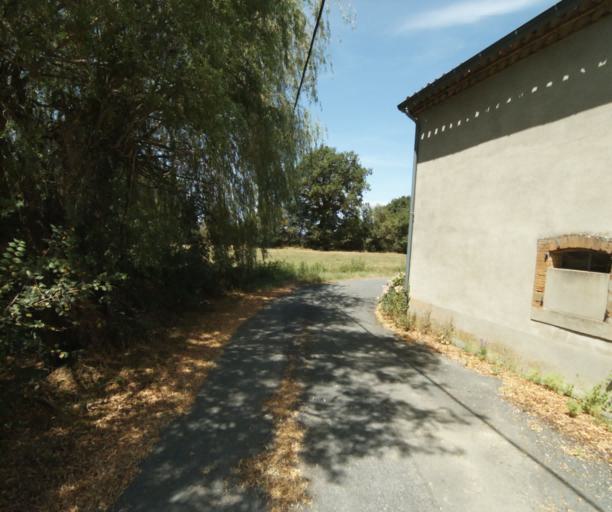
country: FR
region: Midi-Pyrenees
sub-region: Departement du Tarn
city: Soreze
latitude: 43.4924
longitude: 2.0568
